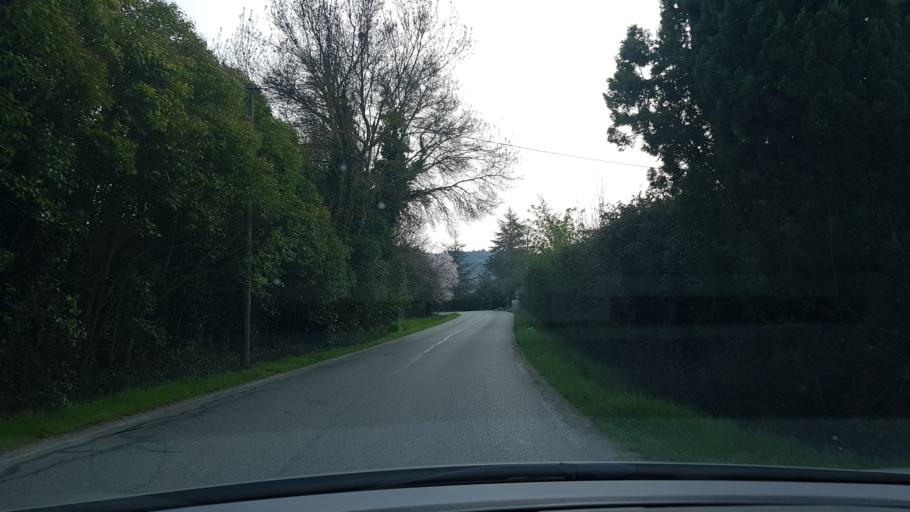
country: FR
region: Provence-Alpes-Cote d'Azur
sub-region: Departement des Bouches-du-Rhone
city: Simiane-Collongue
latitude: 43.4362
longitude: 5.4378
